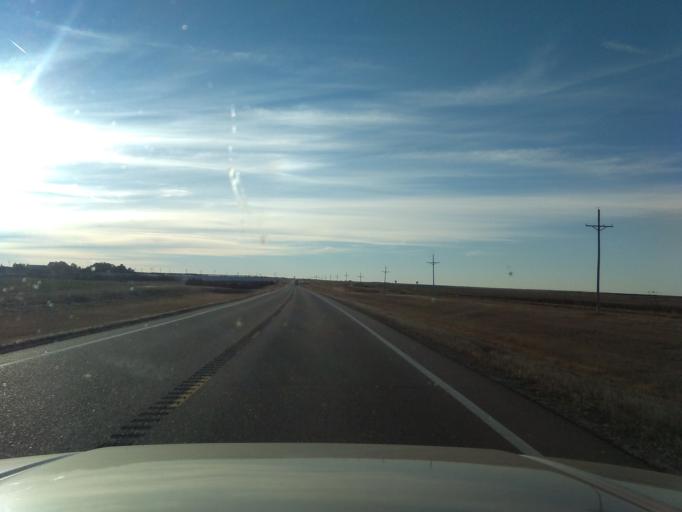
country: US
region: Kansas
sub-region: Thomas County
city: Colby
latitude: 39.4476
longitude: -100.8220
